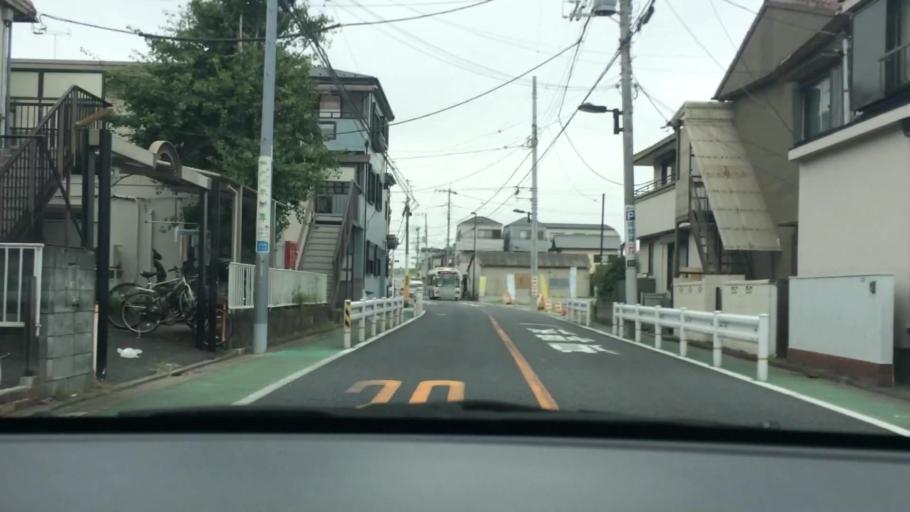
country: JP
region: Chiba
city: Matsudo
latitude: 35.7444
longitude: 139.8911
